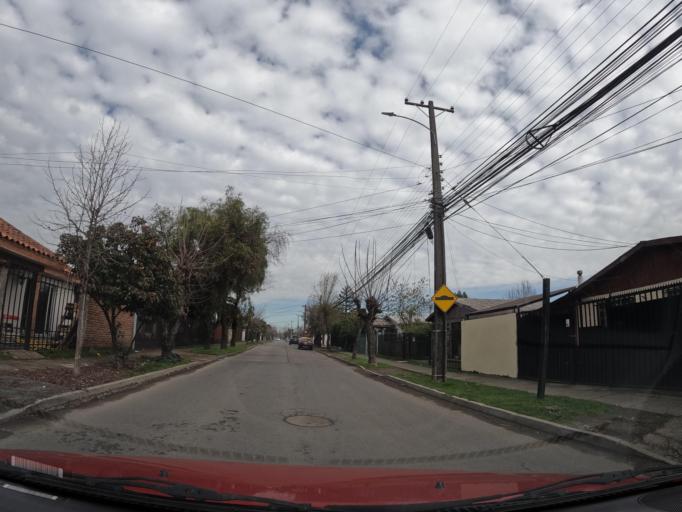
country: CL
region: Maule
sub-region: Provincia de Linares
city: Linares
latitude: -35.8372
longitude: -71.6024
